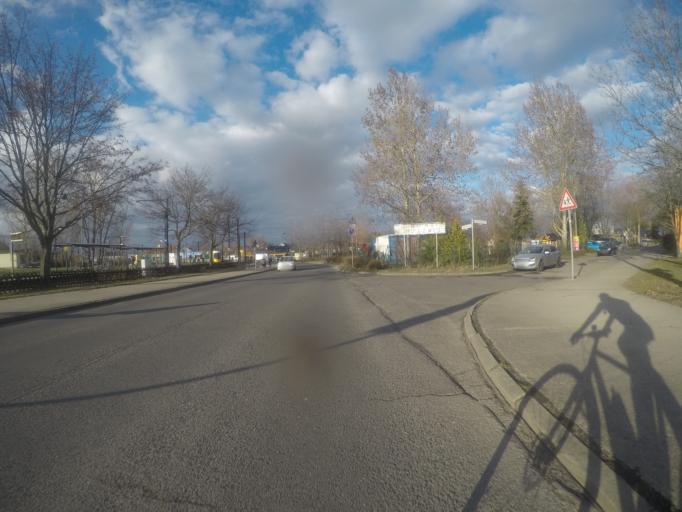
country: DE
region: Brandenburg
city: Ahrensfelde
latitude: 52.5726
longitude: 13.5751
